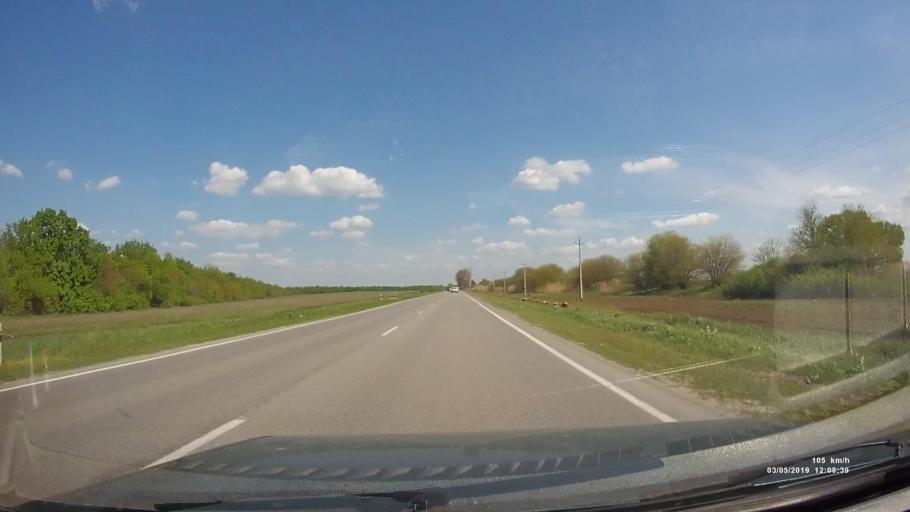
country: RU
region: Rostov
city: Bagayevskaya
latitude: 47.2890
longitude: 40.5006
